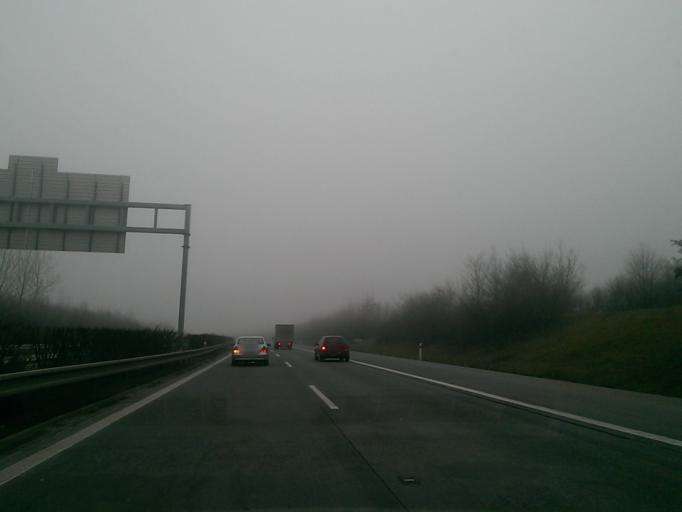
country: CZ
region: Olomoucky
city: Hnevotin
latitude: 49.5575
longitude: 17.2241
